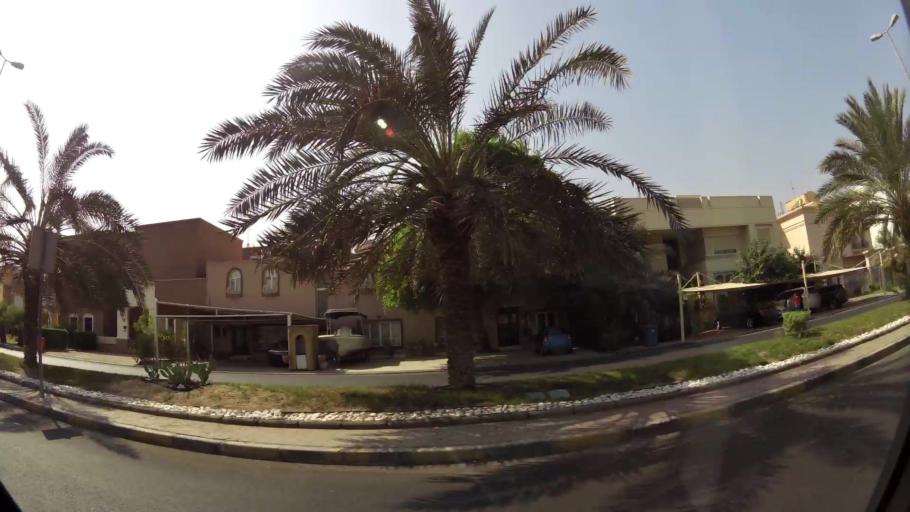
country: KW
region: Al Asimah
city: Ad Dasmah
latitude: 29.3480
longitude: 48.0004
